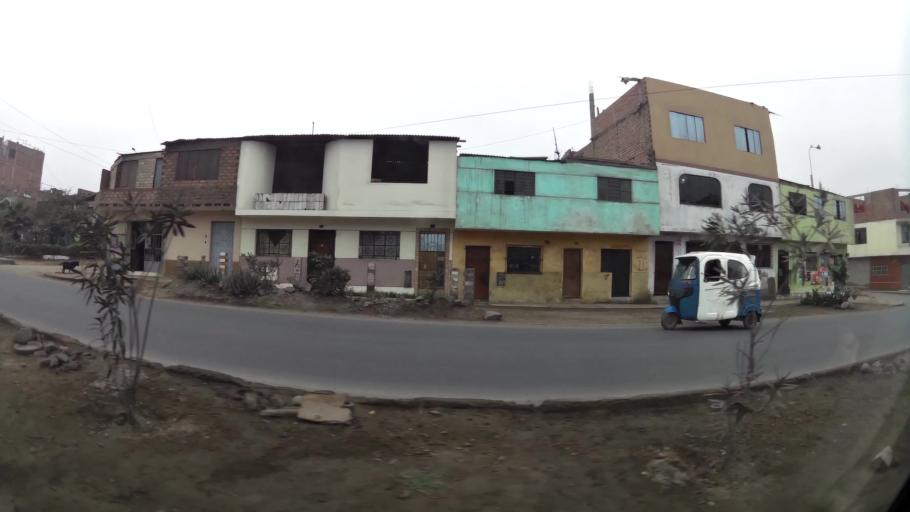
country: PE
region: Lima
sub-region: Lima
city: Urb. Santo Domingo
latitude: -11.9156
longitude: -77.0364
